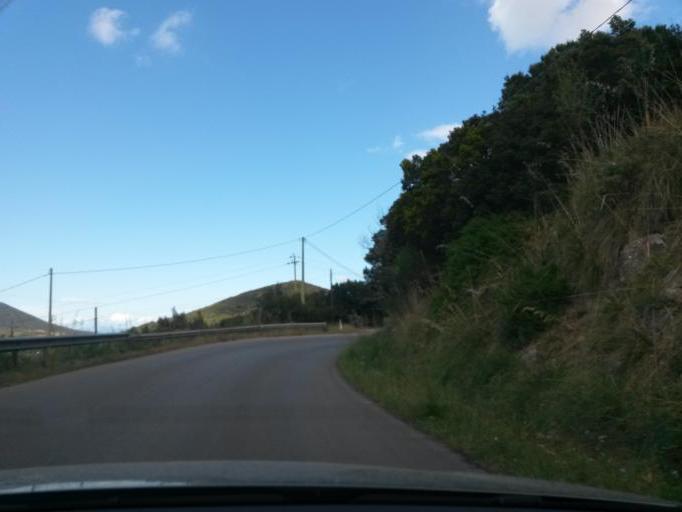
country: IT
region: Tuscany
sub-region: Provincia di Livorno
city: Rio nell'Elba
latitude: 42.7949
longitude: 10.4069
